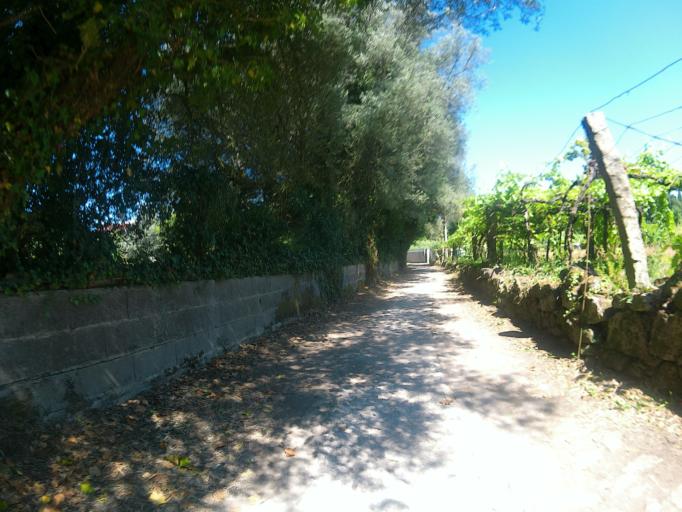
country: PT
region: Viana do Castelo
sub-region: Ponte de Lima
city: Ponte de Lima
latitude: 41.7640
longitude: -8.6070
